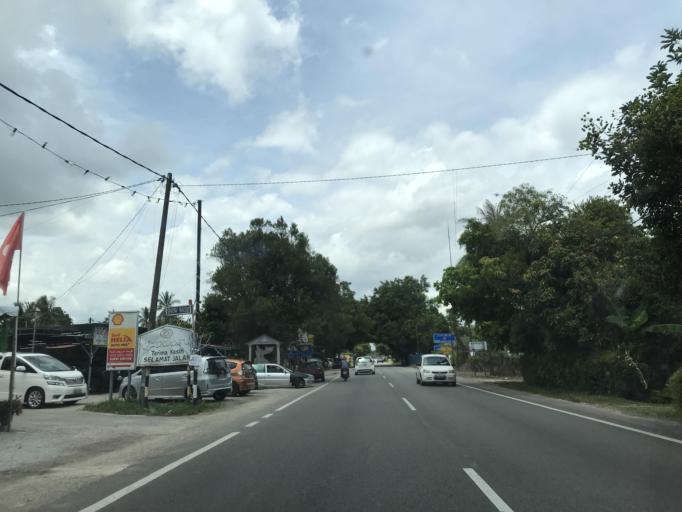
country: MY
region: Kelantan
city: Kota Bharu
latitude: 6.0893
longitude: 102.2078
